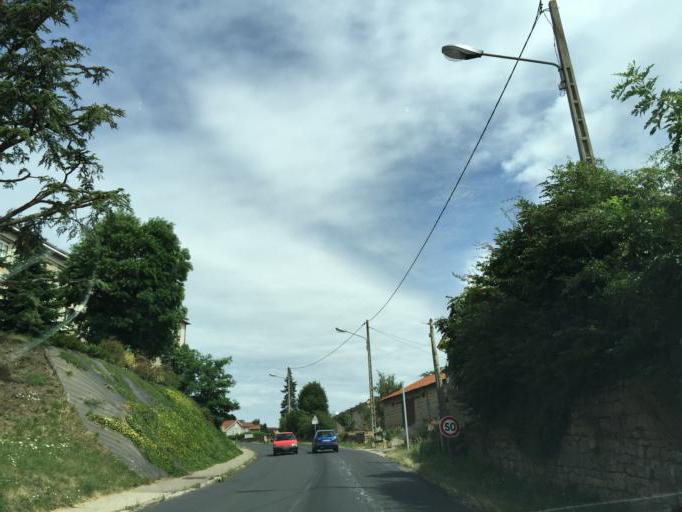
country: FR
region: Rhone-Alpes
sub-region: Departement de la Loire
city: Saint-Bonnet-le-Chateau
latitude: 45.4205
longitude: 4.0691
